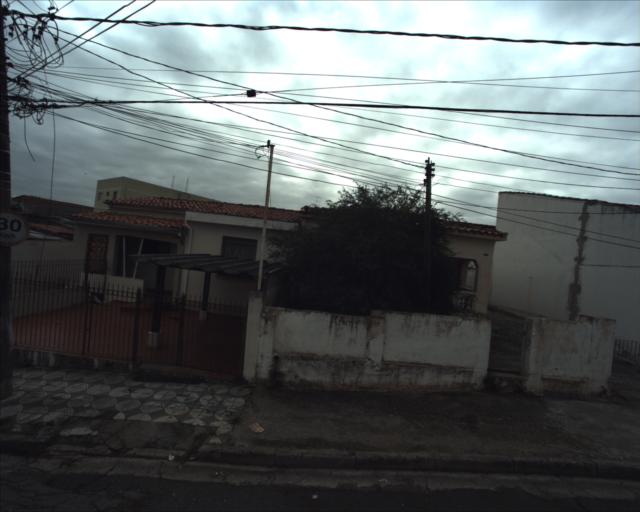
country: BR
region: Sao Paulo
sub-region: Sorocaba
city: Sorocaba
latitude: -23.5024
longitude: -47.4361
